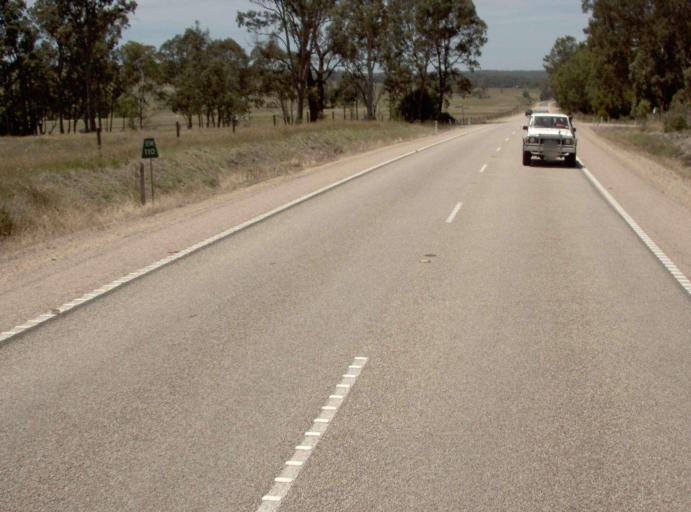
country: AU
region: Victoria
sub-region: East Gippsland
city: Bairnsdale
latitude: -37.7642
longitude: 147.6991
